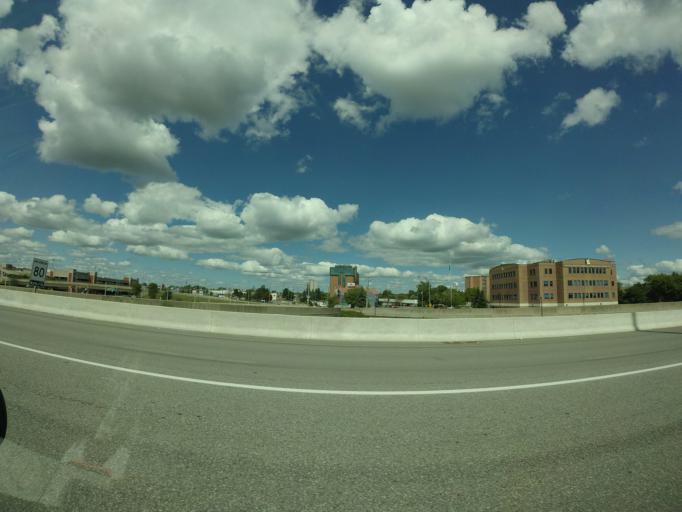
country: CA
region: Ontario
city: Ottawa
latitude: 45.4204
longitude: -75.6341
